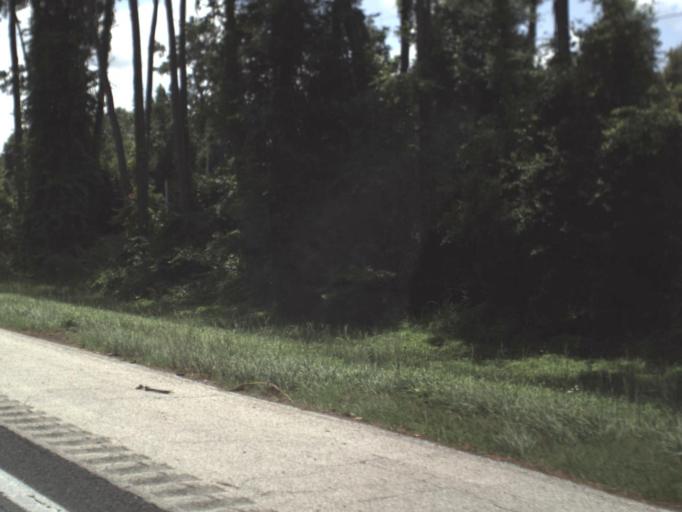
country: US
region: Florida
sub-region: Alachua County
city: Alachua
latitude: 29.7208
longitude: -82.4686
